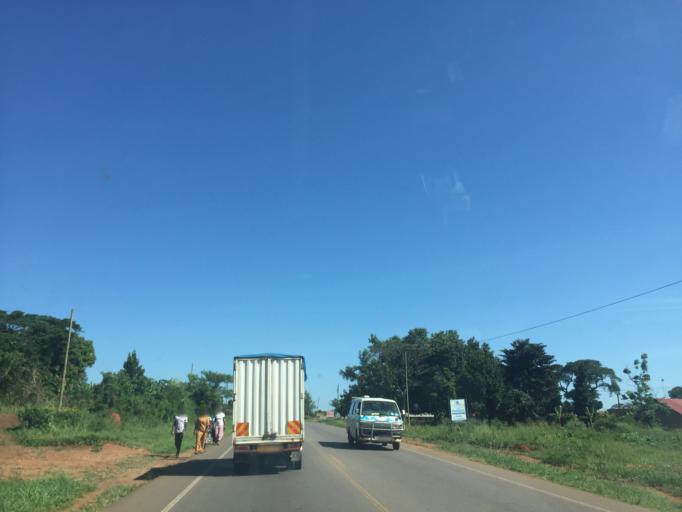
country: UG
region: Central Region
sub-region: Luwero District
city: Wobulenzi
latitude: 0.7803
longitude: 32.5105
